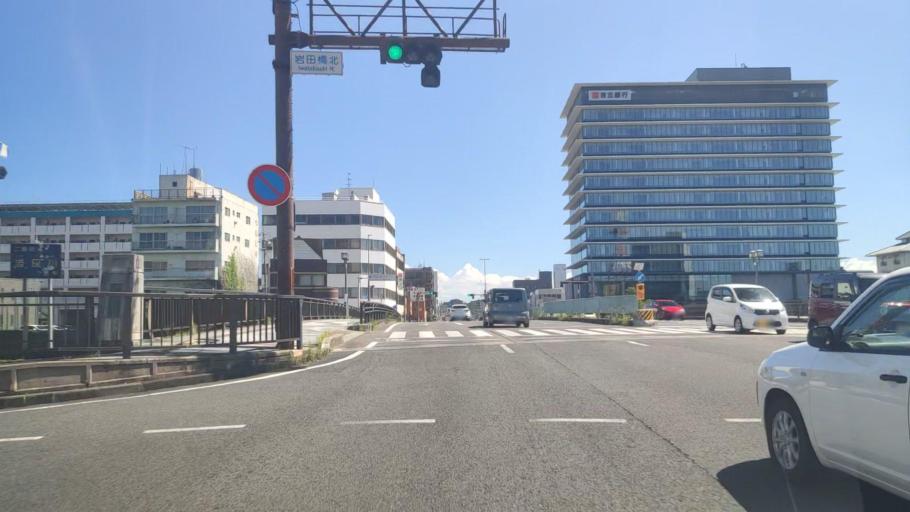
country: JP
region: Mie
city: Tsu-shi
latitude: 34.7142
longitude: 136.5092
